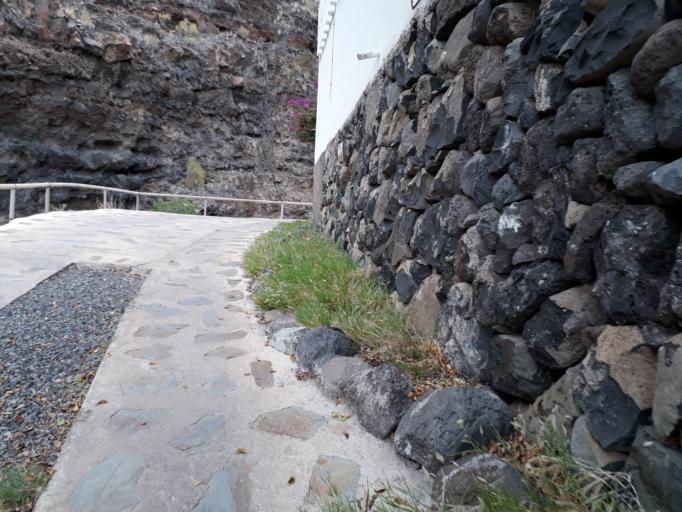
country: ES
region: Canary Islands
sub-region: Provincia de Santa Cruz de Tenerife
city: Alajero
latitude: 28.0807
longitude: -17.3232
